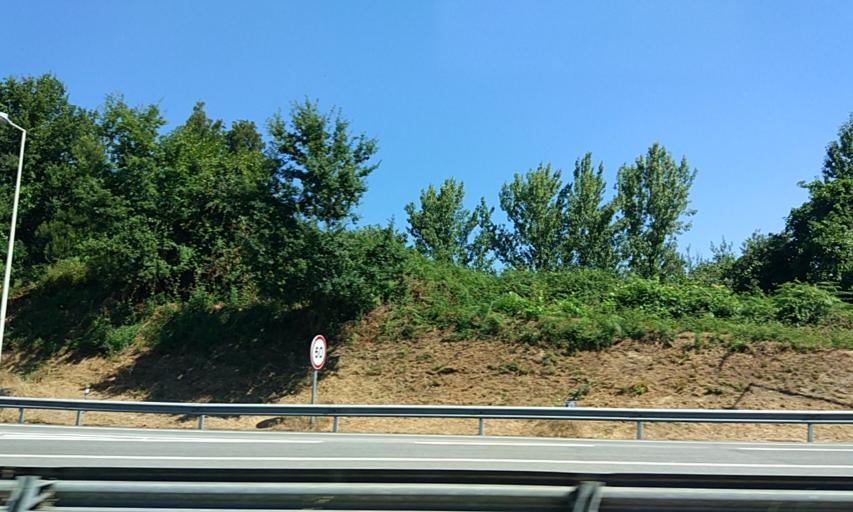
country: PT
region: Porto
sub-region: Lousada
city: Meinedo
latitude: 41.2310
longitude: -8.2041
